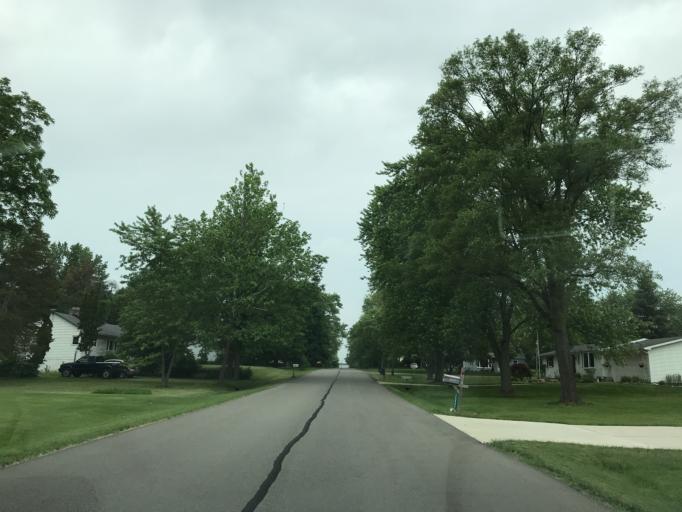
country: US
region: Michigan
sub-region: Oakland County
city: Novi
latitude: 42.4774
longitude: -83.4841
